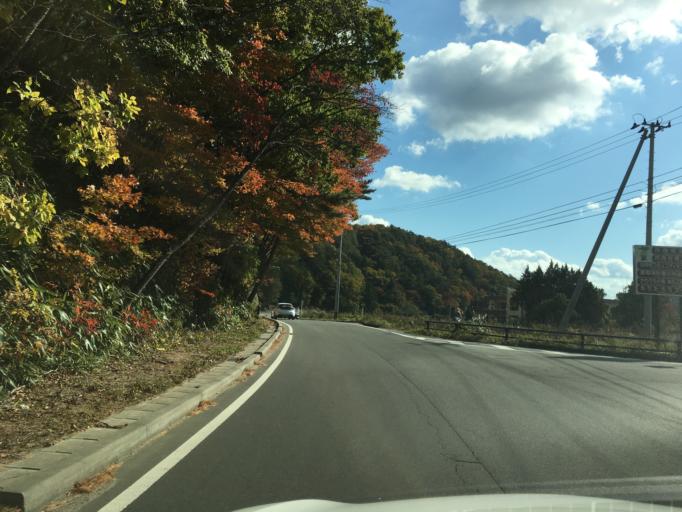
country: JP
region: Fukushima
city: Namie
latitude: 37.3391
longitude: 140.8082
